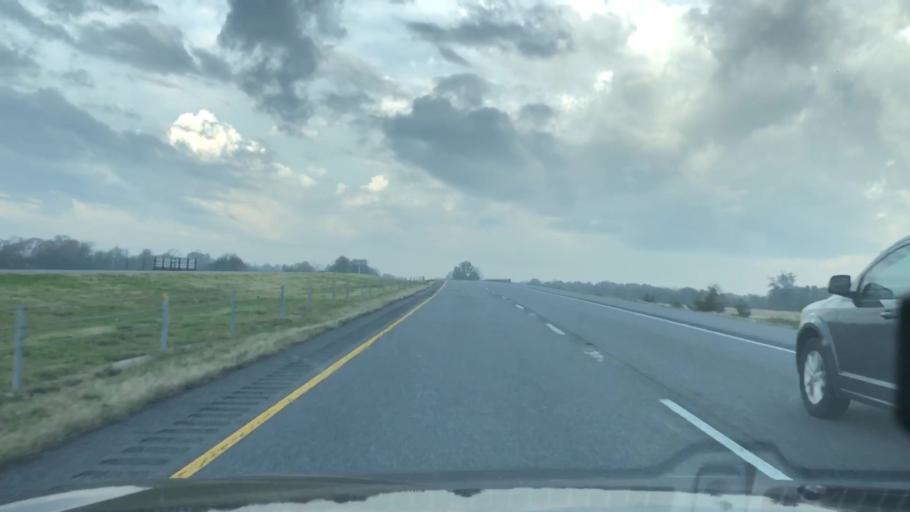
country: US
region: Louisiana
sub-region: Madison Parish
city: Tallulah
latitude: 32.4045
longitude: -91.2239
